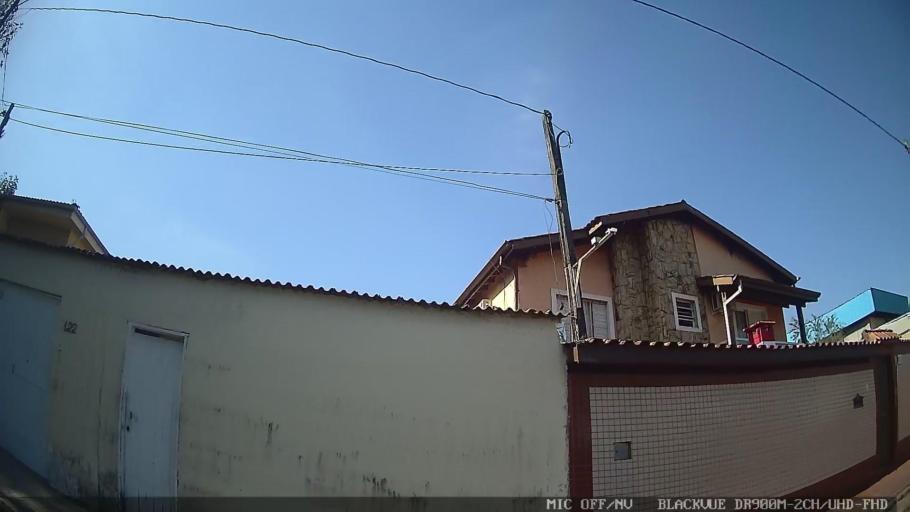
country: BR
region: Sao Paulo
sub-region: Santos
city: Santos
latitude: -23.9364
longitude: -46.3061
